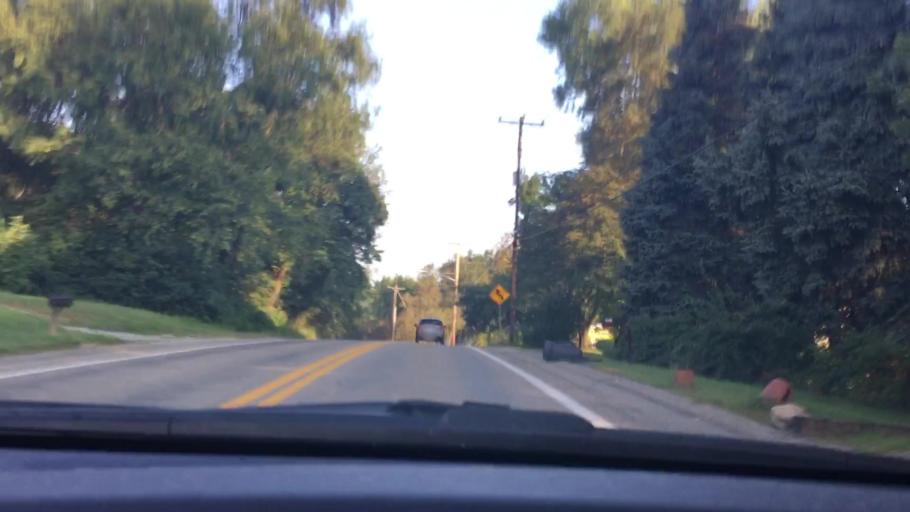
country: US
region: Pennsylvania
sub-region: Allegheny County
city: Lincoln
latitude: 40.3195
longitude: -79.8639
